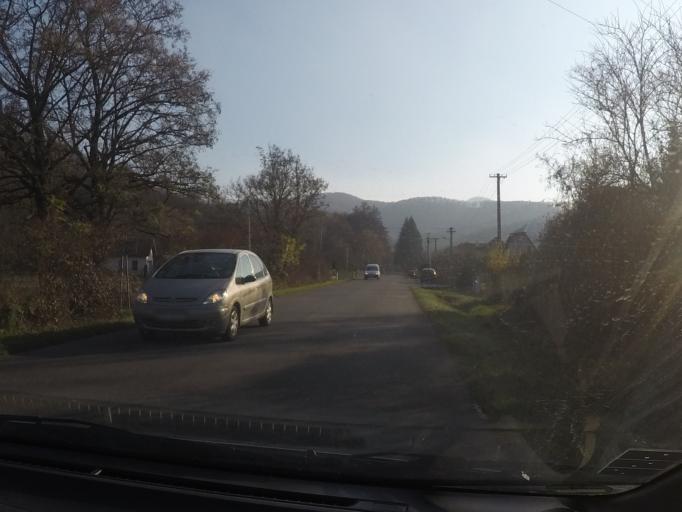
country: SK
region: Banskobystricky
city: Zarnovica
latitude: 48.4705
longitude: 18.7249
